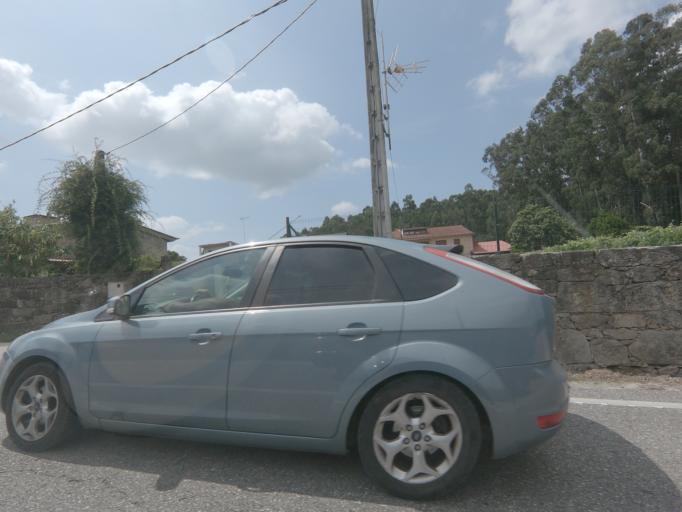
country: PT
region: Viana do Castelo
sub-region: Valenca
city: Valenca
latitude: 42.0265
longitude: -8.6769
